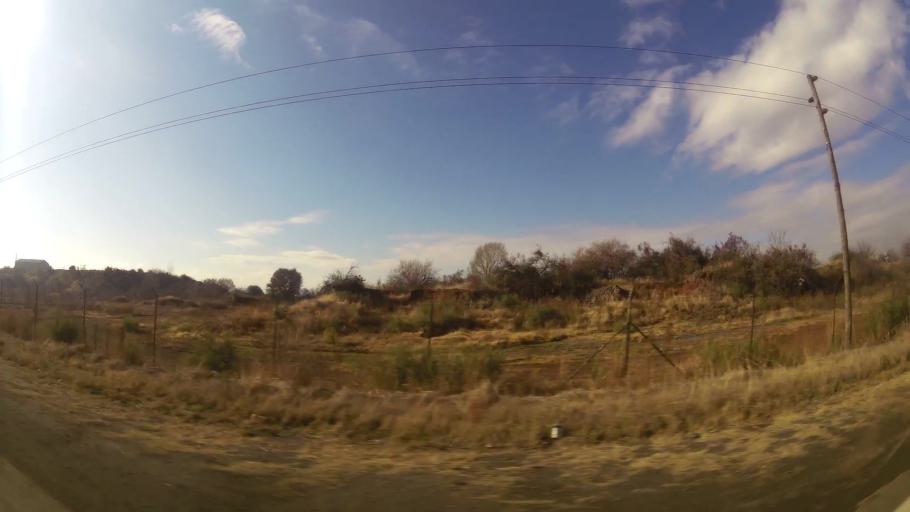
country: ZA
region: Gauteng
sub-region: Sedibeng District Municipality
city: Meyerton
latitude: -26.5137
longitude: 28.0515
